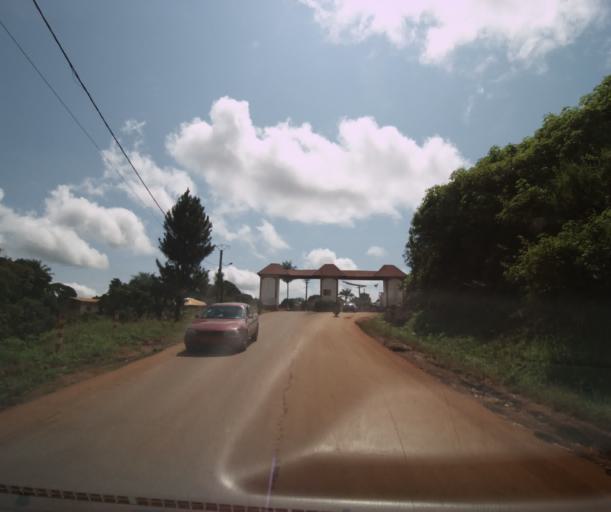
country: CM
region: West
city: Foumban
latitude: 5.7319
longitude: 10.8817
